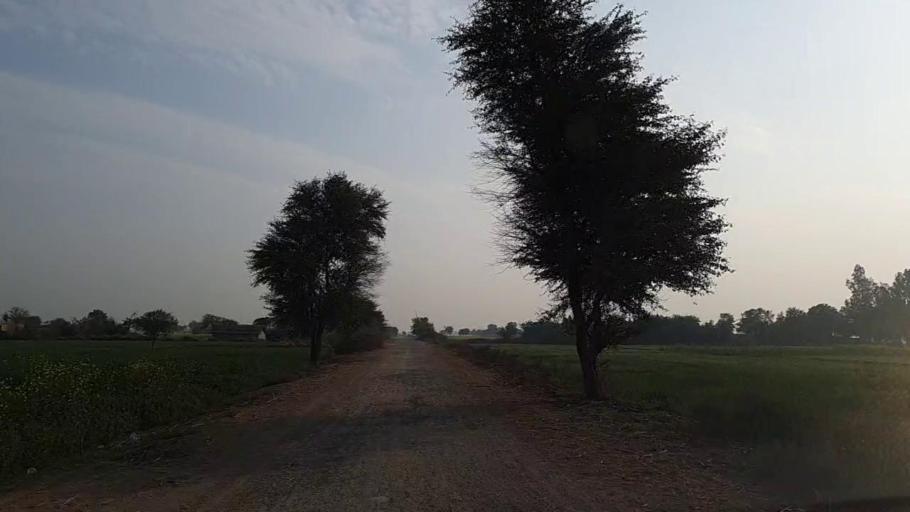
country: PK
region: Sindh
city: Jam Sahib
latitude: 26.3257
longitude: 68.5338
